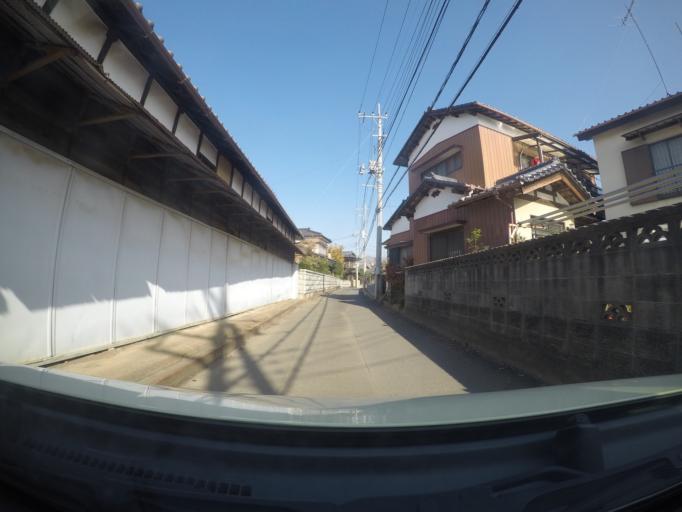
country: JP
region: Ibaraki
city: Tsukuba
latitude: 36.1262
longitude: 140.1210
